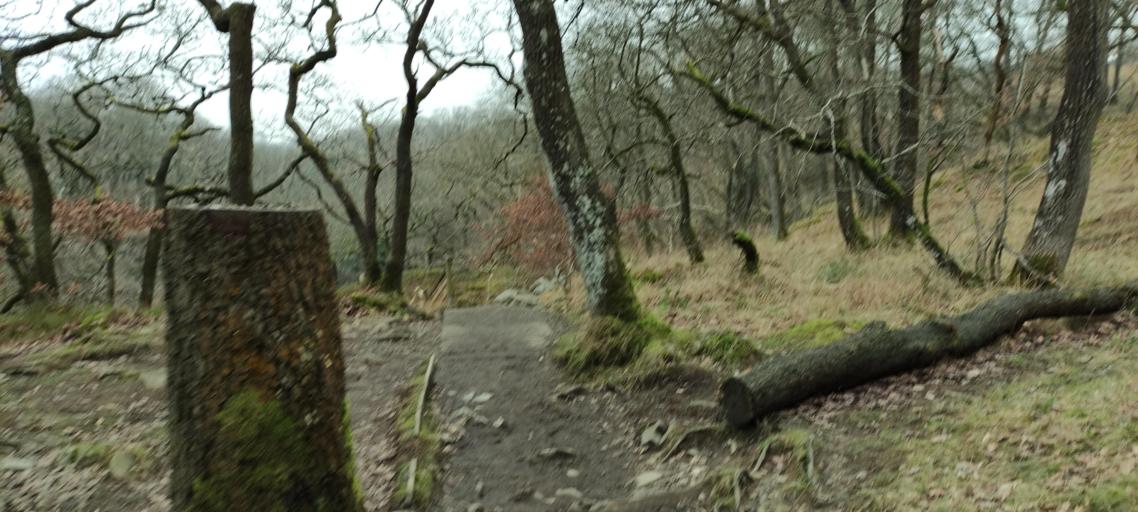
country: GB
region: England
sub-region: North Yorkshire
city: Ingleton
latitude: 54.1649
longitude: -2.4548
